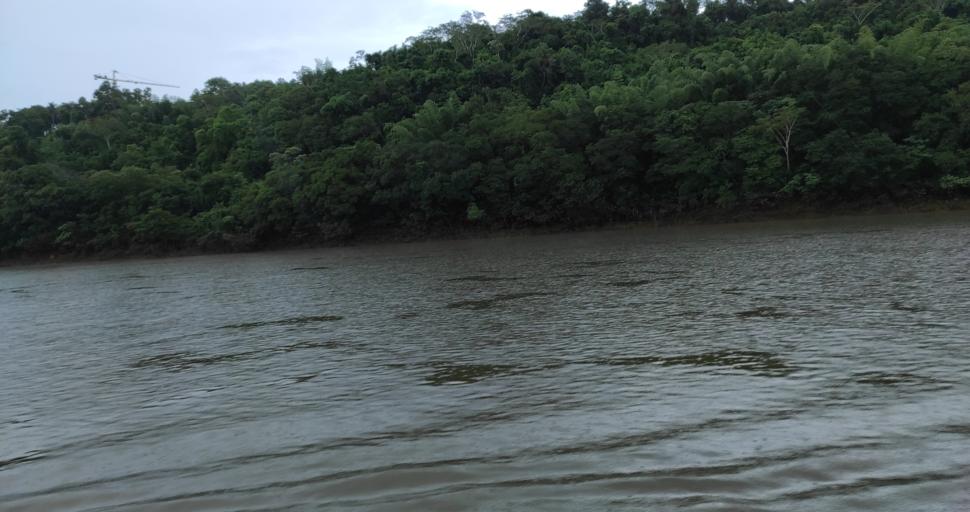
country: AR
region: Misiones
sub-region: Departamento de Iguazu
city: Puerto Iguazu
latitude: -25.5927
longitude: -54.5876
